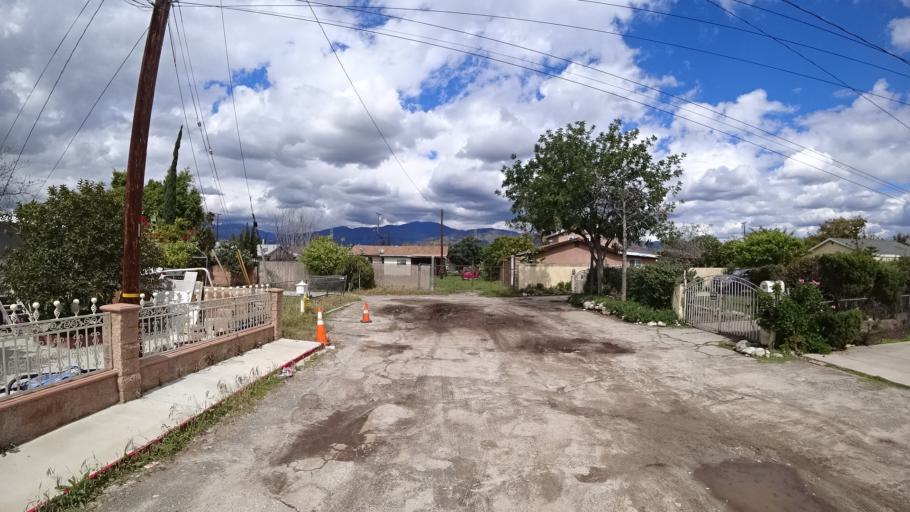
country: US
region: California
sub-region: Los Angeles County
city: Baldwin Park
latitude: 34.1030
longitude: -117.9594
